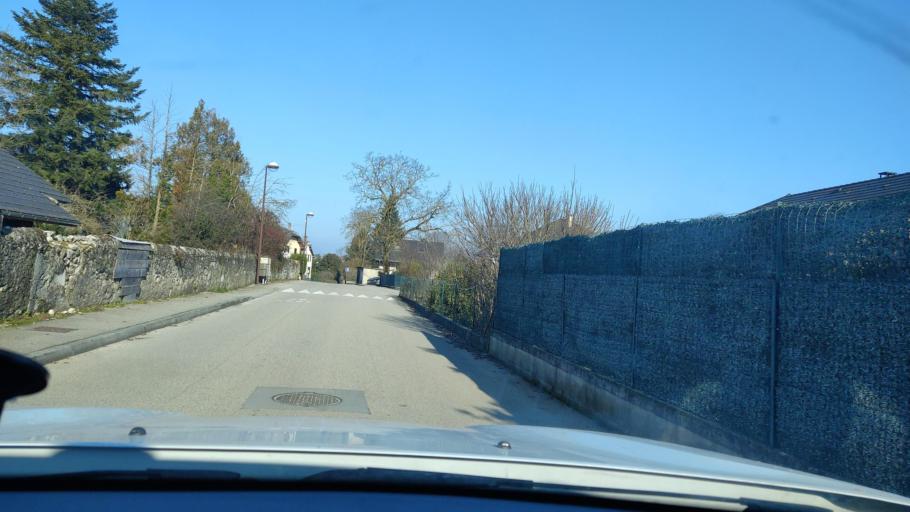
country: FR
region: Rhone-Alpes
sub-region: Departement de la Savoie
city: Viviers-du-Lac
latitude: 45.6442
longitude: 5.9042
